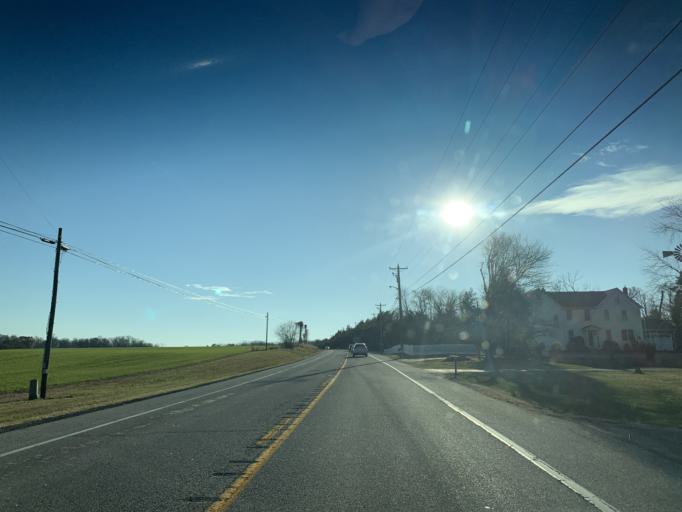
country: US
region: Delaware
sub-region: New Castle County
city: Middletown
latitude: 39.3795
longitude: -75.8792
